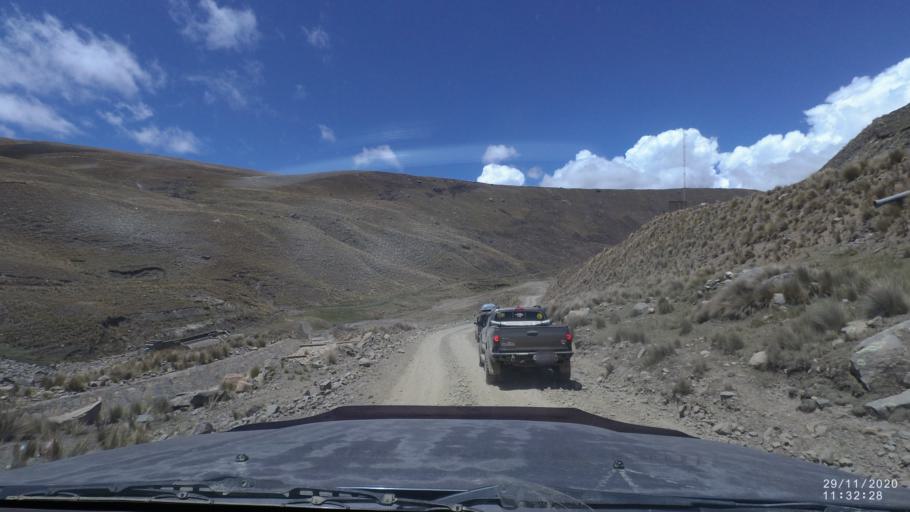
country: BO
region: Cochabamba
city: Cochabamba
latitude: -17.1854
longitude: -66.2096
